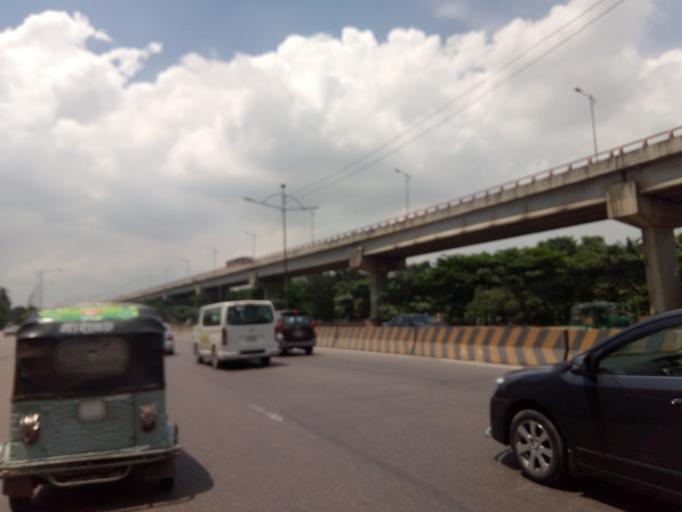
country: BD
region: Dhaka
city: Tungi
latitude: 23.8150
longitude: 90.4046
